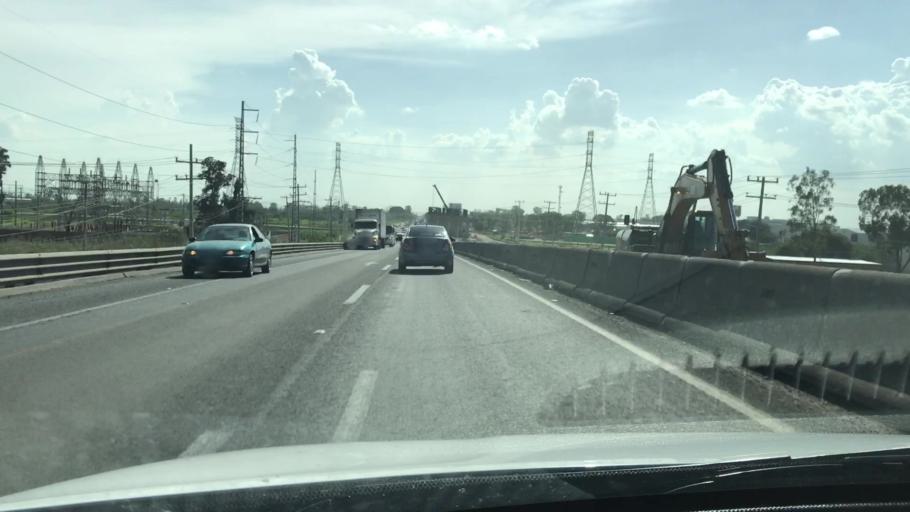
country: MX
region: Guanajuato
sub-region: Celaya
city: Colonia Fraccionamiento el Puente
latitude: 20.5152
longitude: -100.8964
